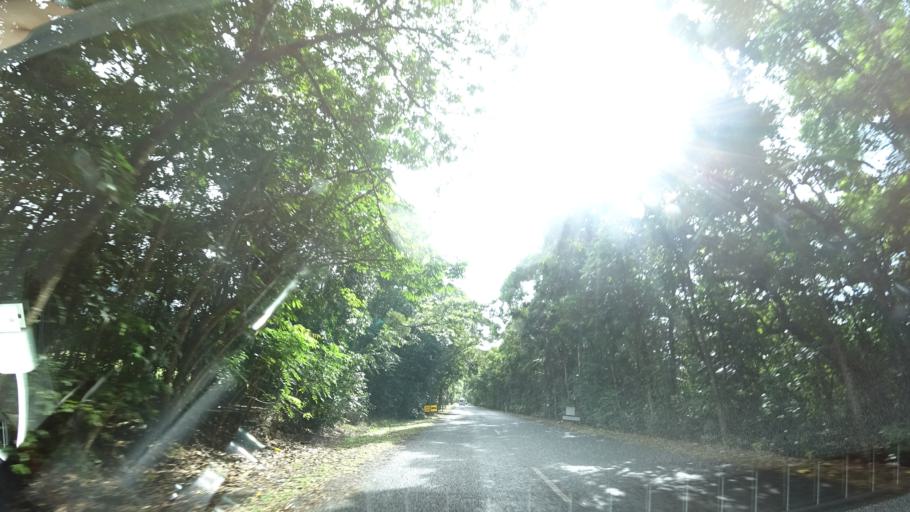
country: AU
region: Queensland
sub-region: Cairns
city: Port Douglas
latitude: -16.0949
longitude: 145.4599
